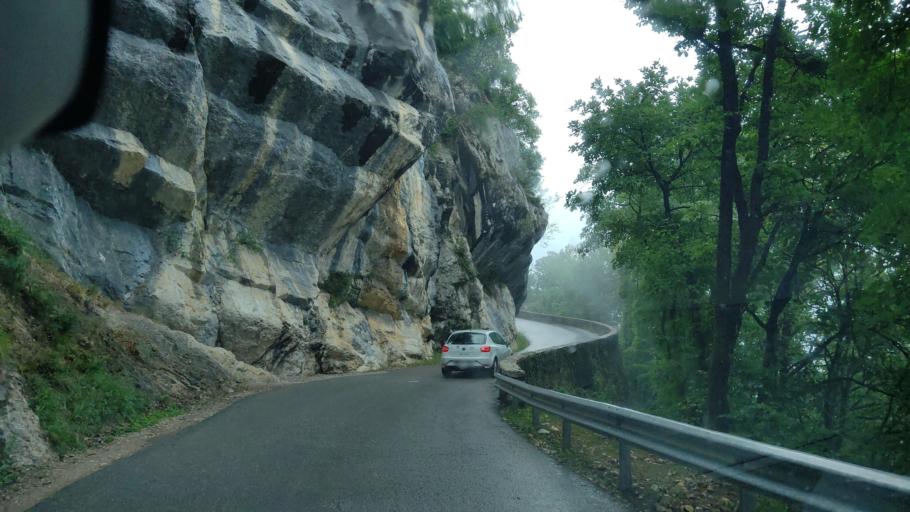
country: FR
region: Rhone-Alpes
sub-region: Departement de la Savoie
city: Chatillon
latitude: 45.7871
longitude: 5.8652
